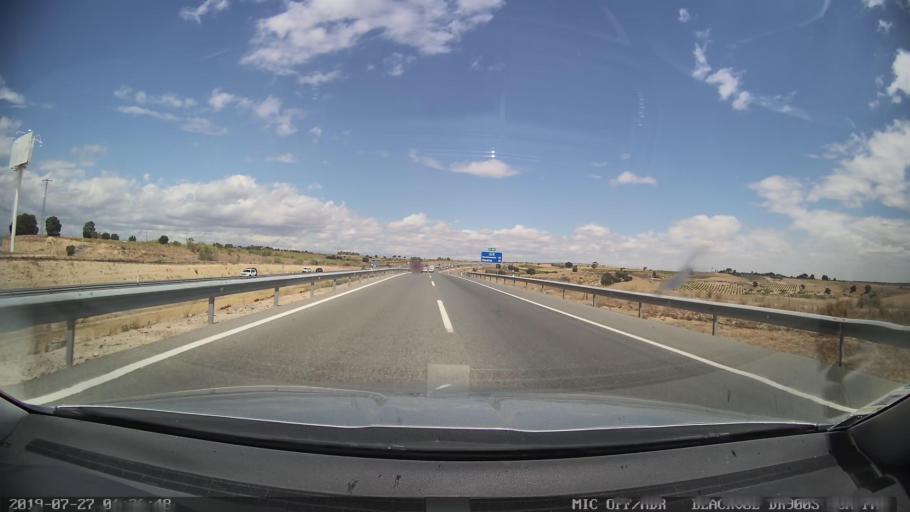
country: ES
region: Castille-La Mancha
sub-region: Province of Toledo
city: La Torre de Esteban Hambran
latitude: 40.1634
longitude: -4.1684
